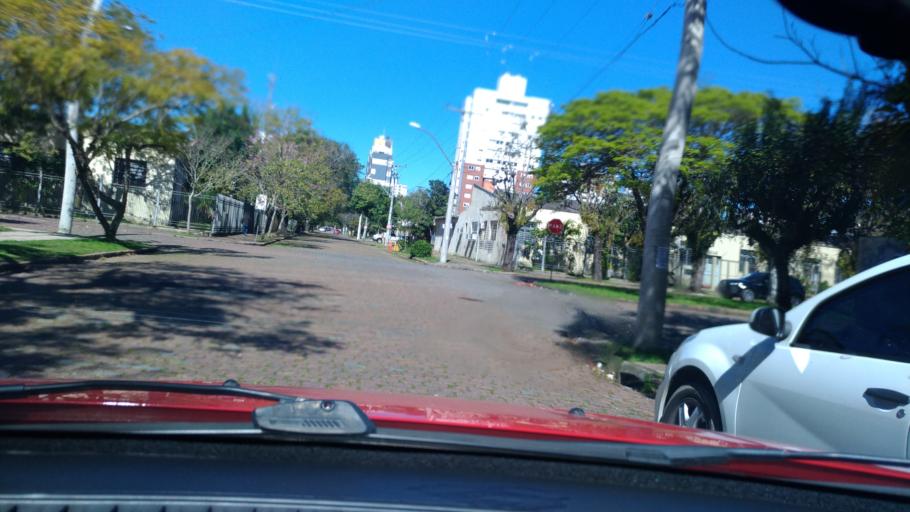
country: BR
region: Rio Grande do Sul
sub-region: Porto Alegre
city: Porto Alegre
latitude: -30.0442
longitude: -51.2016
